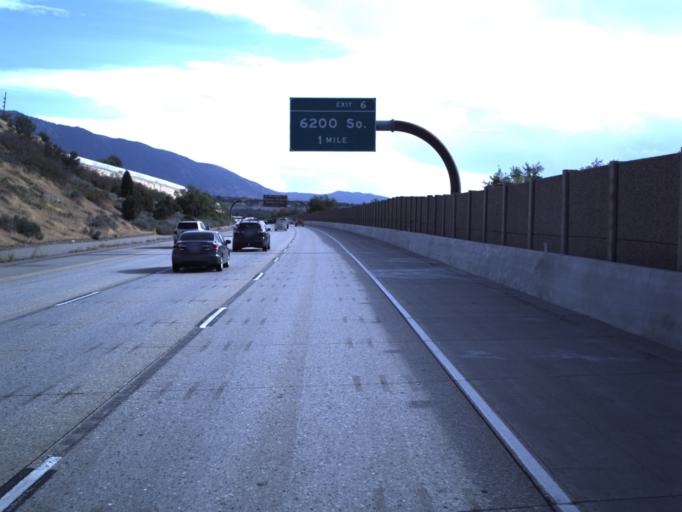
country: US
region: Utah
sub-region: Salt Lake County
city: Holladay
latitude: 40.6552
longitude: -111.8077
